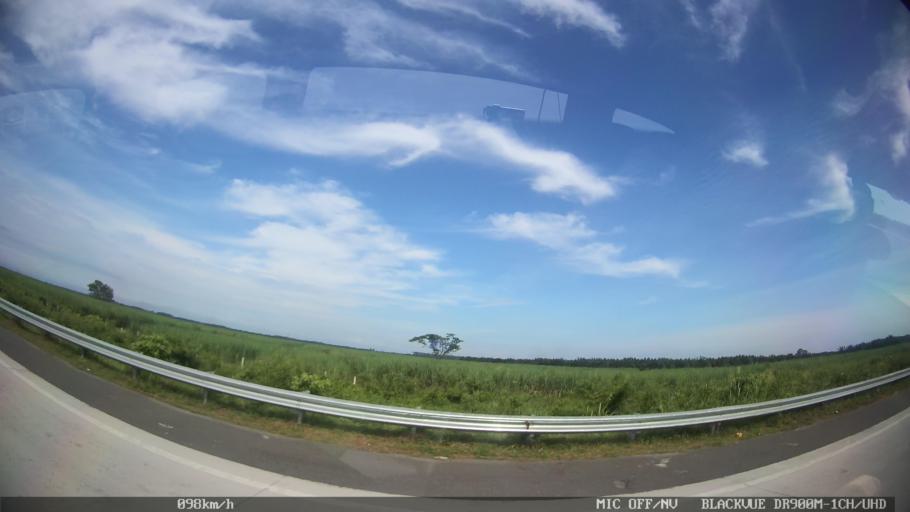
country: ID
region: North Sumatra
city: Binjai
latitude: 3.6813
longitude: 98.5373
